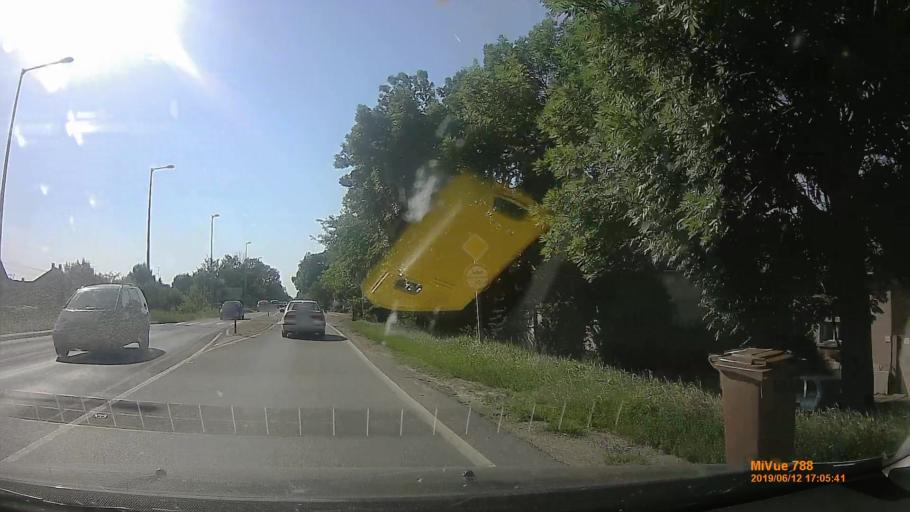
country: HU
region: Csongrad
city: Deszk
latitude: 46.2235
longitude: 20.1928
